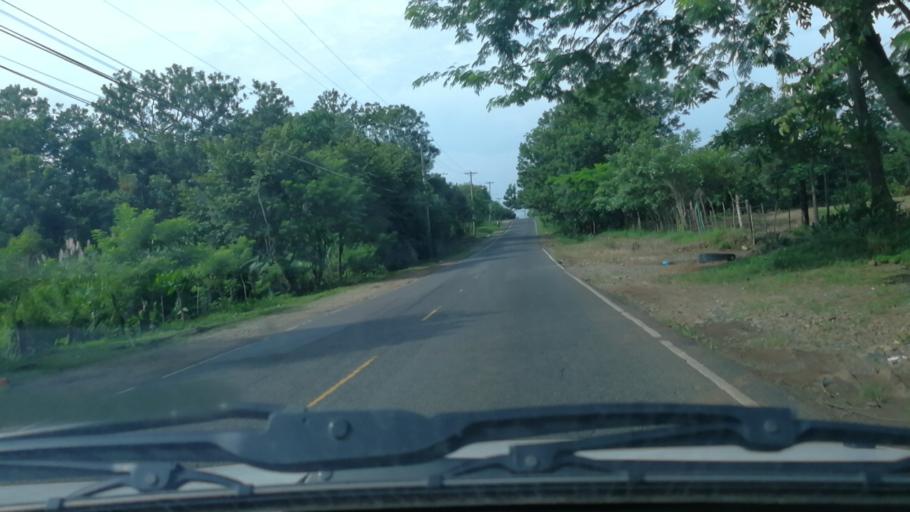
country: PA
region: Panama
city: Pacora
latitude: 9.0941
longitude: -79.2885
